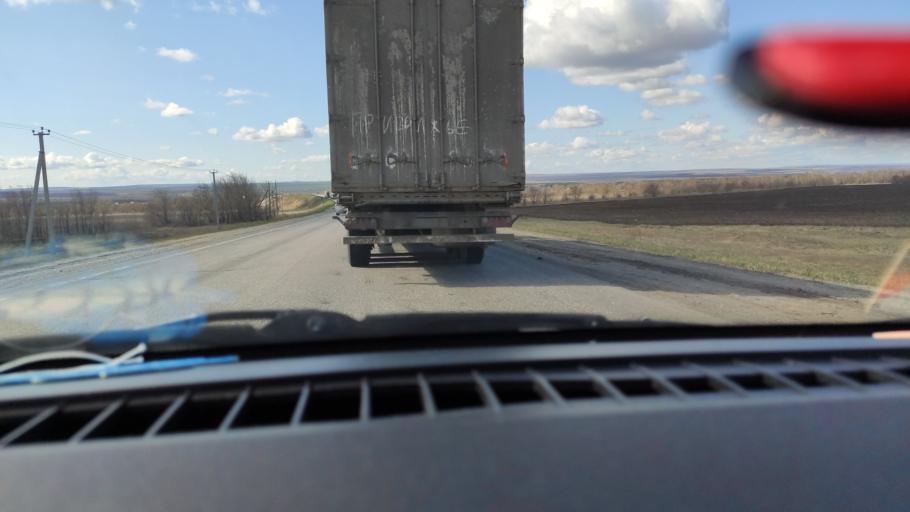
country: RU
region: Samara
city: Varlamovo
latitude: 53.1774
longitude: 48.2836
